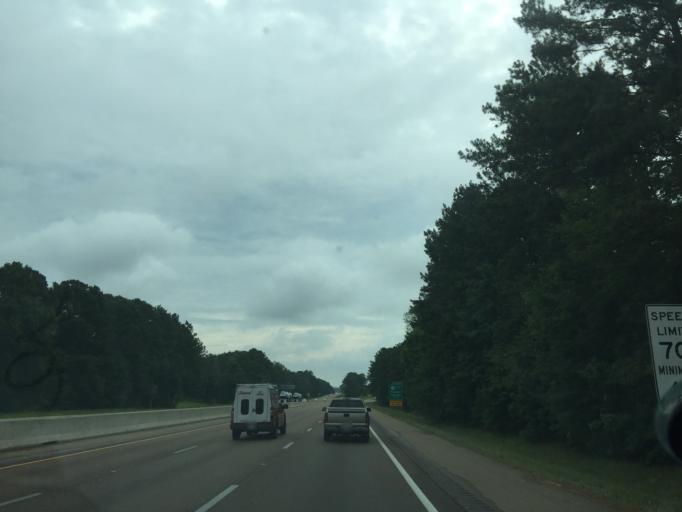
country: US
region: Mississippi
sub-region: Rankin County
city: Pearl
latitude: 32.2731
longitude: -90.0619
